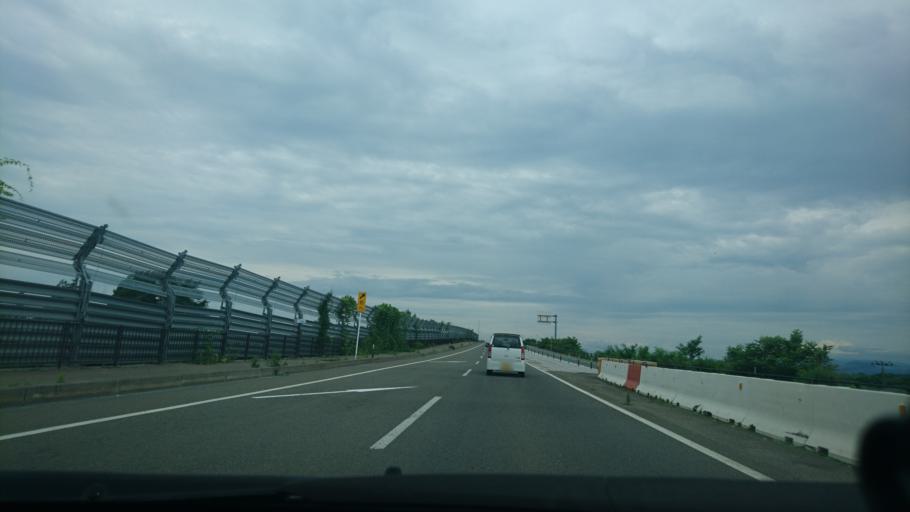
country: JP
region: Akita
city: Omagari
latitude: 39.4886
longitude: 140.4526
